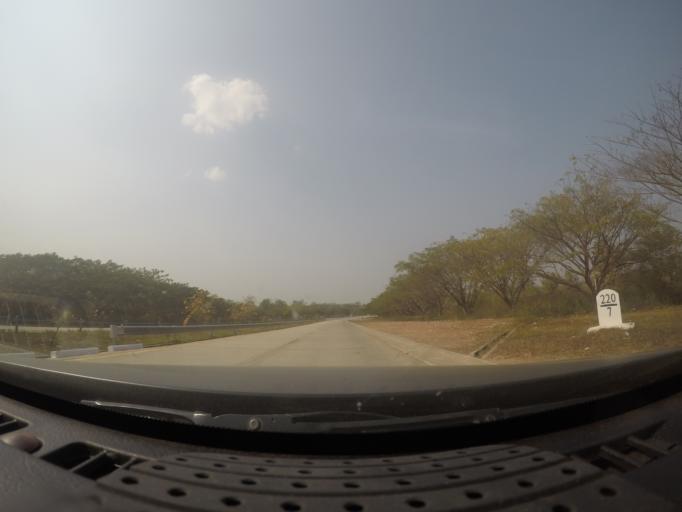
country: MM
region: Mandalay
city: Nay Pyi Taw
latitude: 19.9320
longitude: 95.9863
